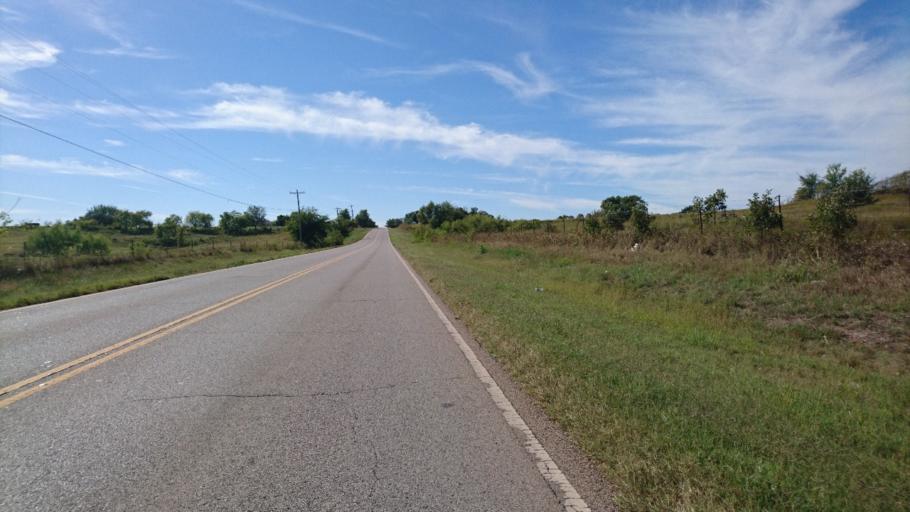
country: US
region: Oklahoma
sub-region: Lincoln County
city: Chandler
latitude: 35.7098
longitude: -96.8077
